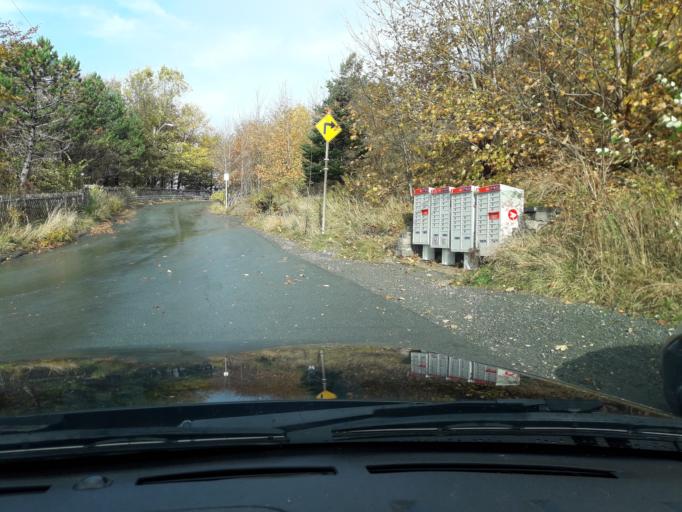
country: CA
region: Newfoundland and Labrador
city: St. John's
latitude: 47.5708
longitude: -52.6944
